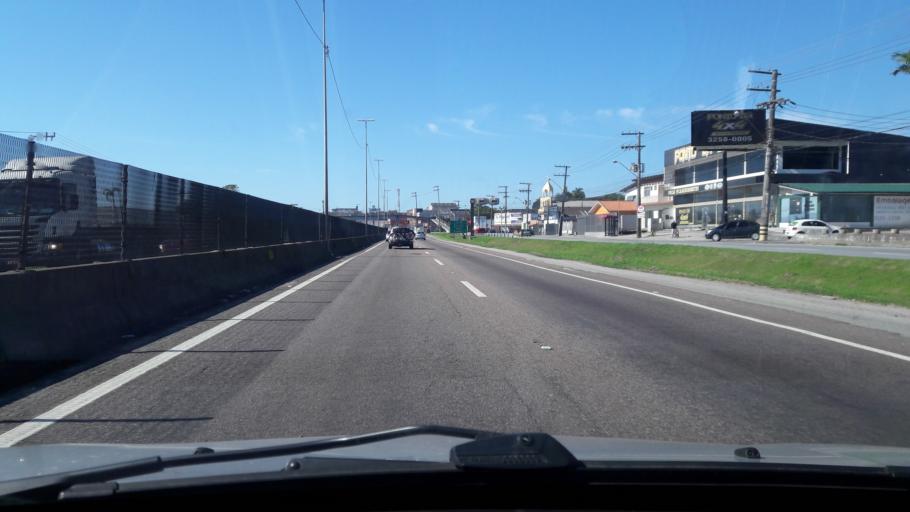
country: BR
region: Santa Catarina
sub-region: Biguacu
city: Biguacu
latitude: -27.5312
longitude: -48.6321
